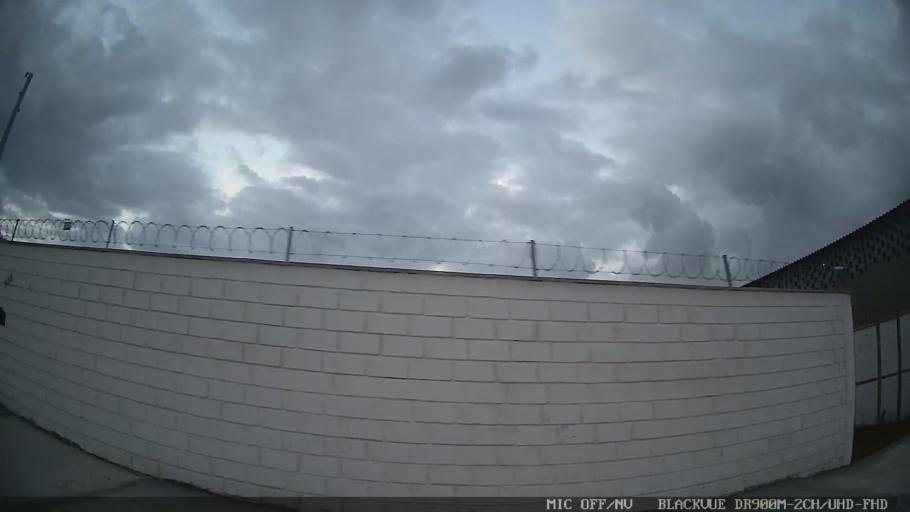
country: BR
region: Sao Paulo
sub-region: Itanhaem
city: Itanhaem
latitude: -24.1886
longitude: -46.8314
